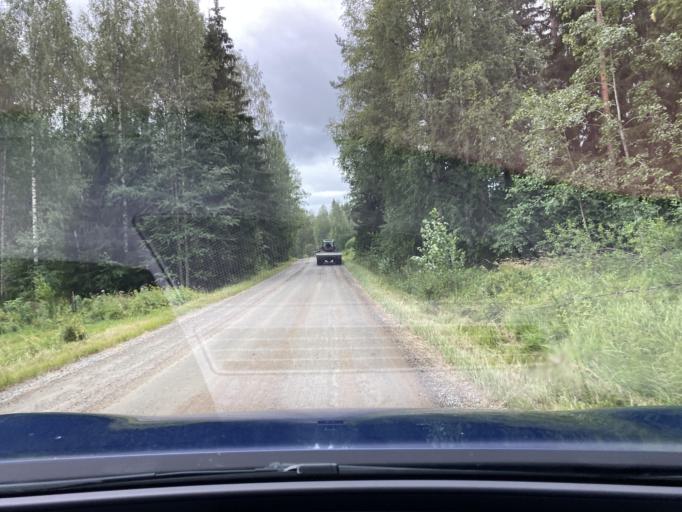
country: FI
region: Pirkanmaa
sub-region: Lounais-Pirkanmaa
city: Punkalaidun
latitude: 61.1766
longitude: 23.1814
